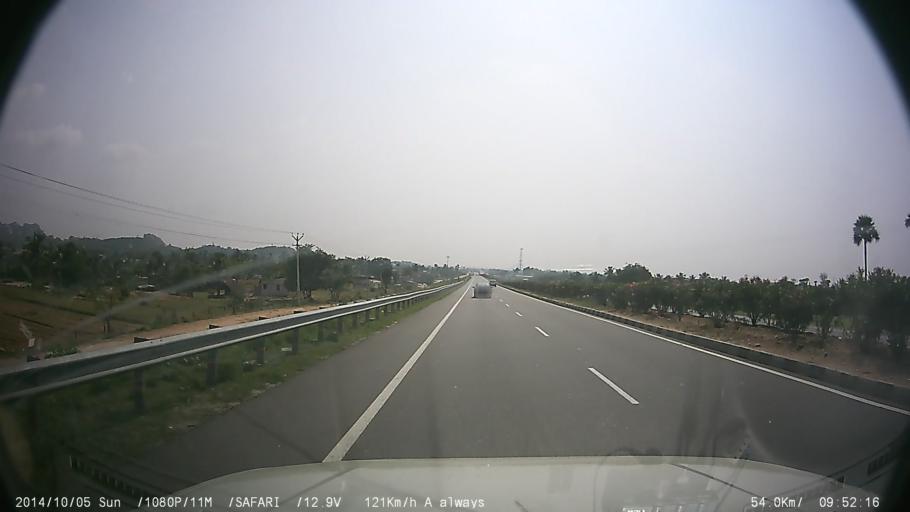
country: IN
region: Tamil Nadu
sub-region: Salem
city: Konganapuram
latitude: 11.4939
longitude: 77.8813
